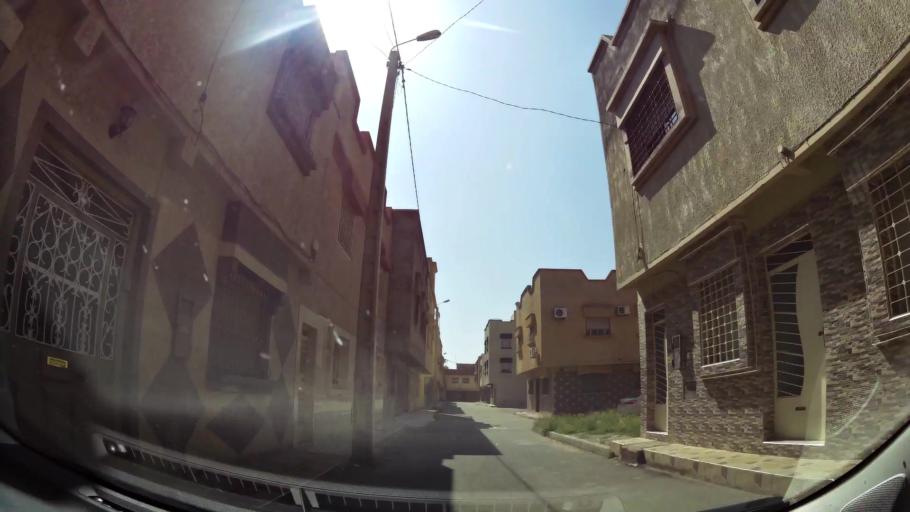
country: MA
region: Oriental
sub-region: Oujda-Angad
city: Oujda
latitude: 34.6770
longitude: -1.9341
